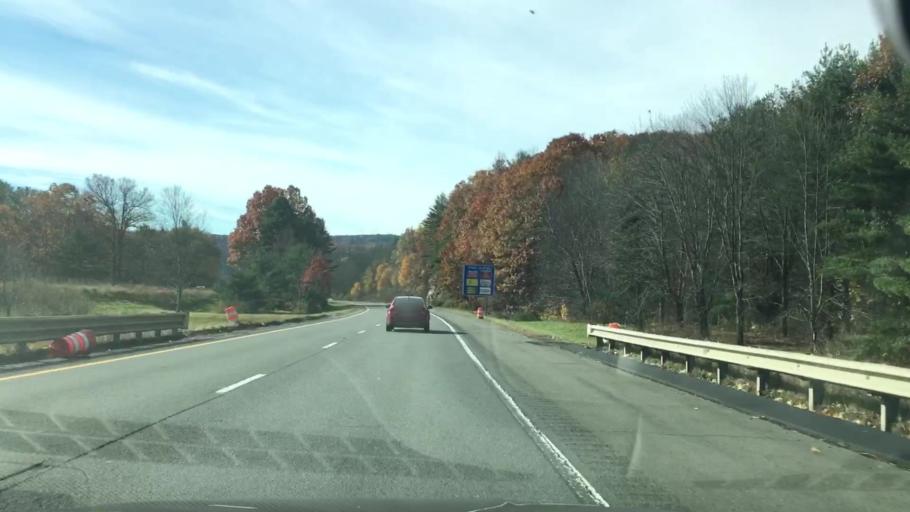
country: US
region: Massachusetts
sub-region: Franklin County
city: Greenfield
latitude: 42.6102
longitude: -72.6076
